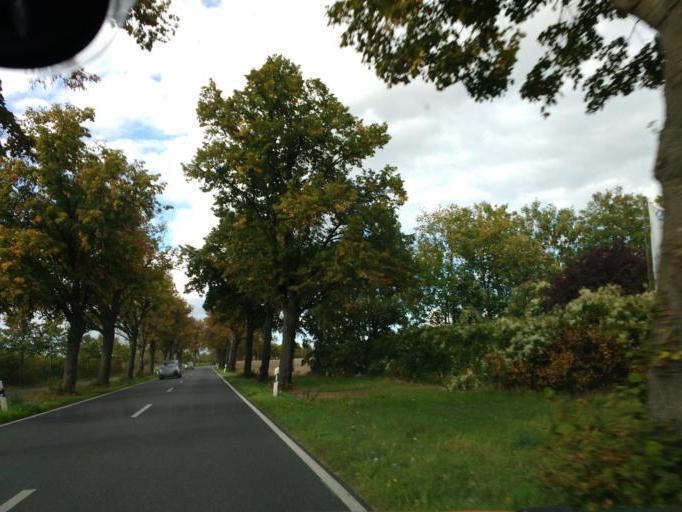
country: DE
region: Berlin
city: Lichtenrade
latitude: 52.3875
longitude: 13.4438
